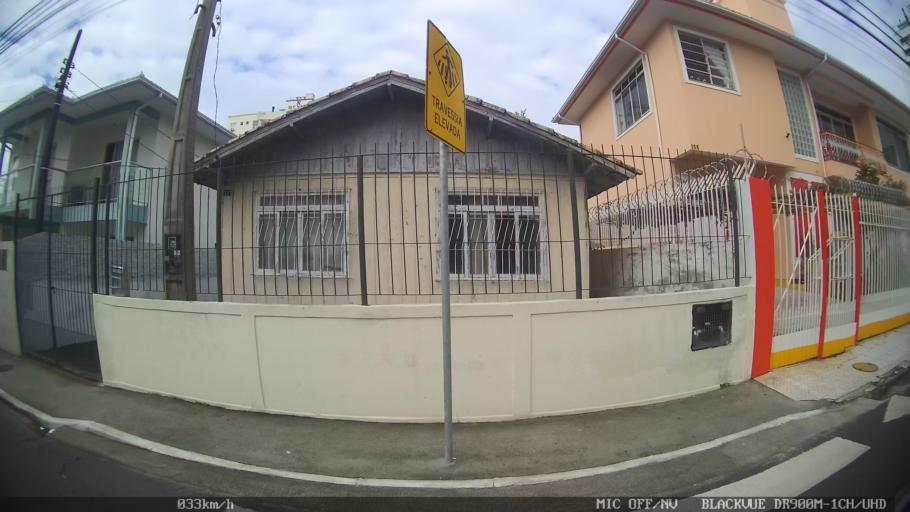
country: BR
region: Santa Catarina
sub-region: Sao Jose
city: Campinas
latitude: -27.5736
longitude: -48.6038
